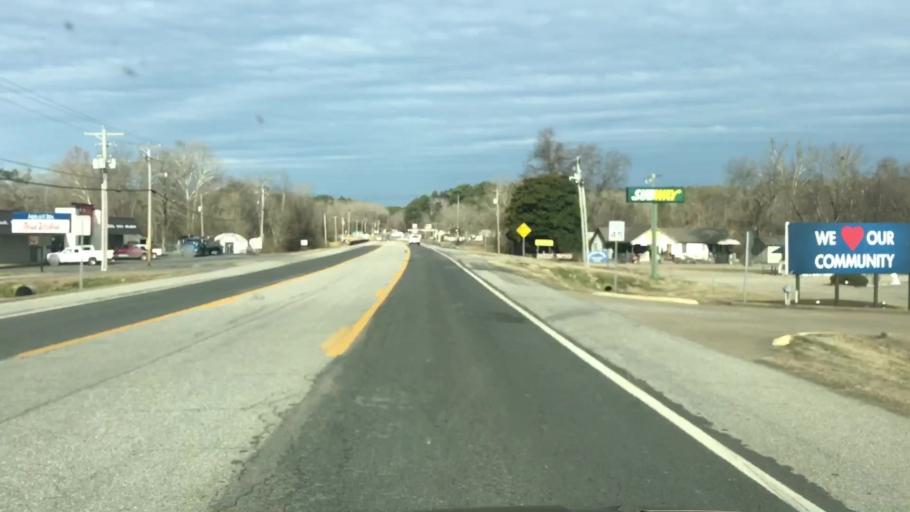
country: US
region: Arkansas
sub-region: Montgomery County
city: Mount Ida
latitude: 34.5593
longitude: -93.6343
